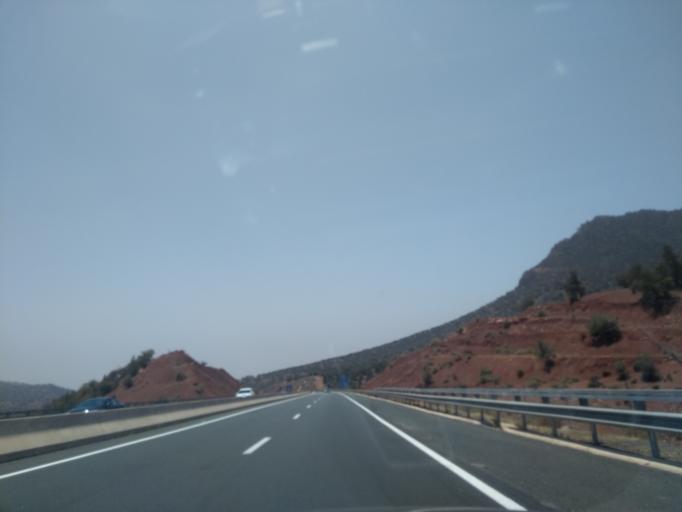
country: MA
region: Souss-Massa-Draa
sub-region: Taroudannt
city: Bigoudine
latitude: 30.5807
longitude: -9.3457
